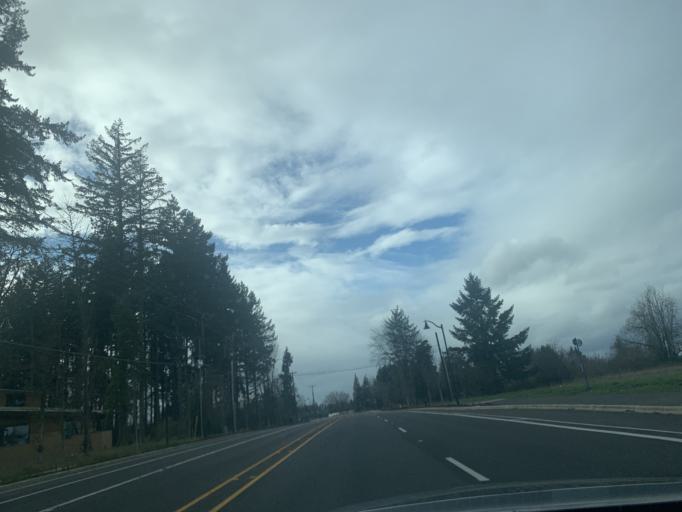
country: US
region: Oregon
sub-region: Washington County
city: Bethany
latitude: 45.5631
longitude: -122.8612
